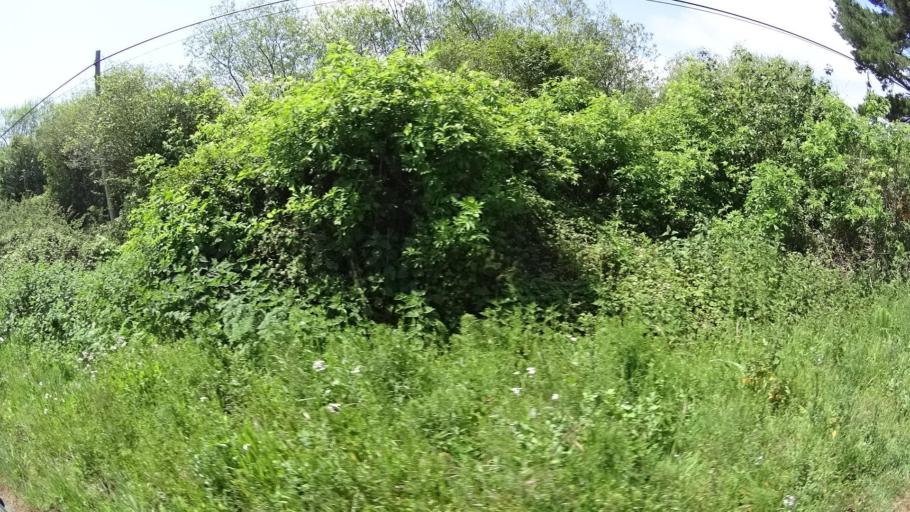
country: US
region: California
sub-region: Humboldt County
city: Ferndale
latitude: 40.6347
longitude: -124.2231
